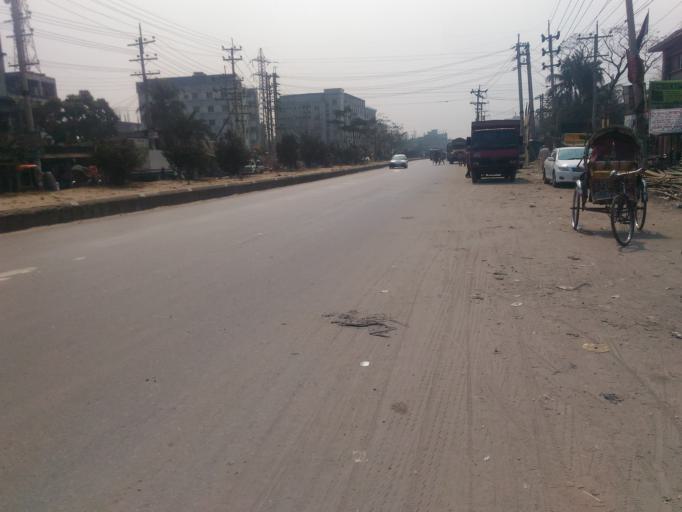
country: BD
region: Dhaka
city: Tungi
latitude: 23.9994
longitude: 90.3826
